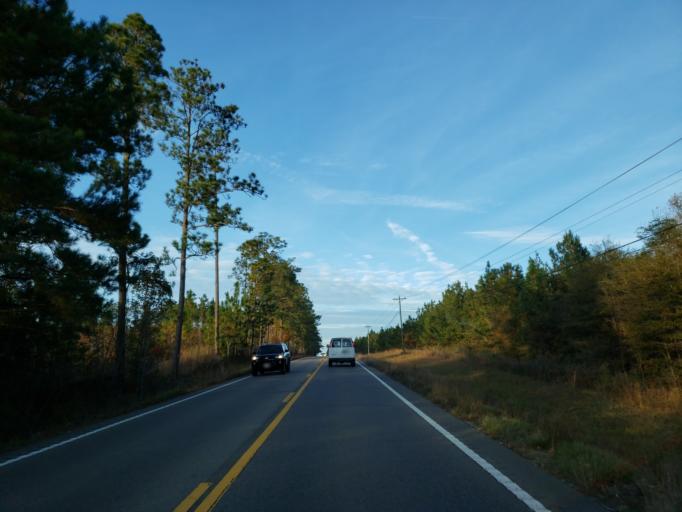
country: US
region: Mississippi
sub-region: Lamar County
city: West Hattiesburg
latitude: 31.2315
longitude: -89.3517
